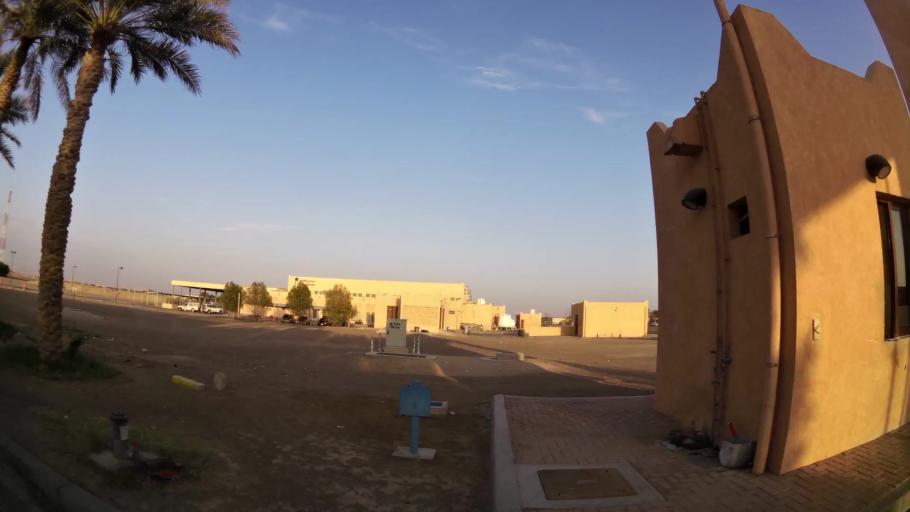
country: AE
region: Abu Dhabi
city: Al Ain
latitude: 24.1600
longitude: 55.8172
